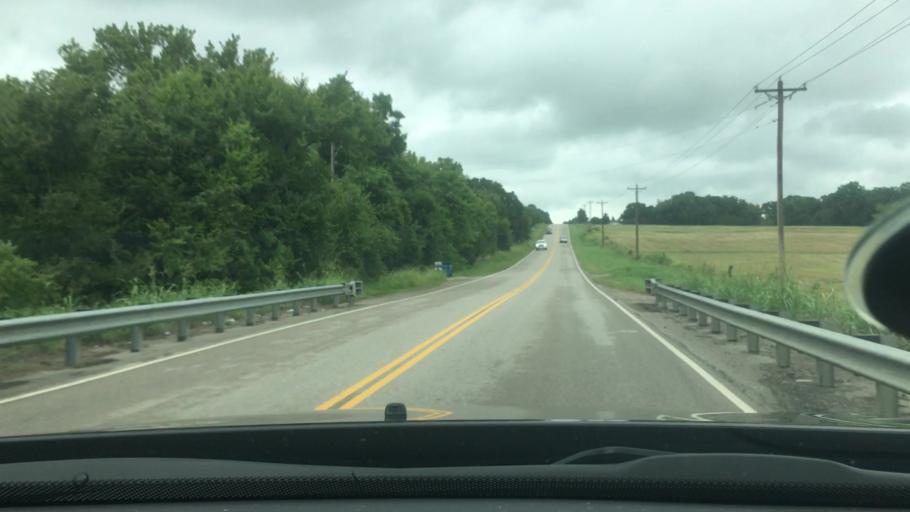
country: US
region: Oklahoma
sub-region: Bryan County
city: Calera
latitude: 33.9757
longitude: -96.5005
